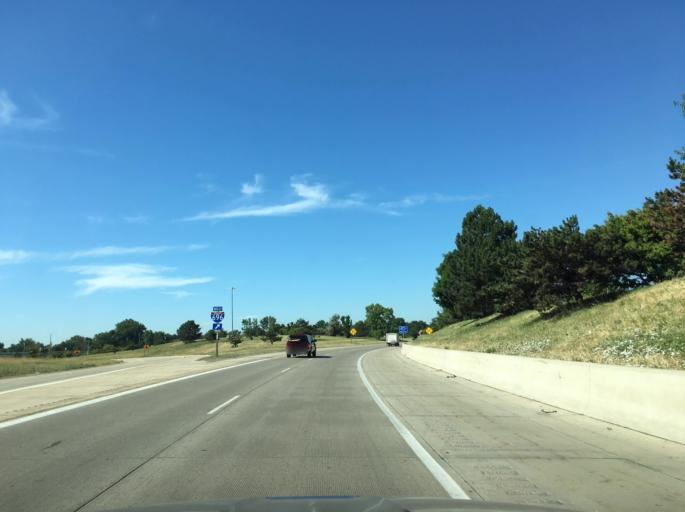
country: US
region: Michigan
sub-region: Macomb County
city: Roseville
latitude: 42.4982
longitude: -82.9188
